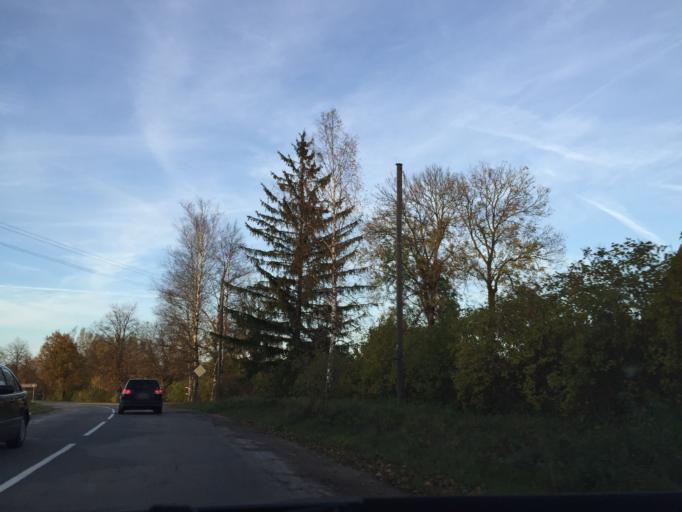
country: LV
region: Malpils
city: Malpils
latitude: 56.8997
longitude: 24.9292
